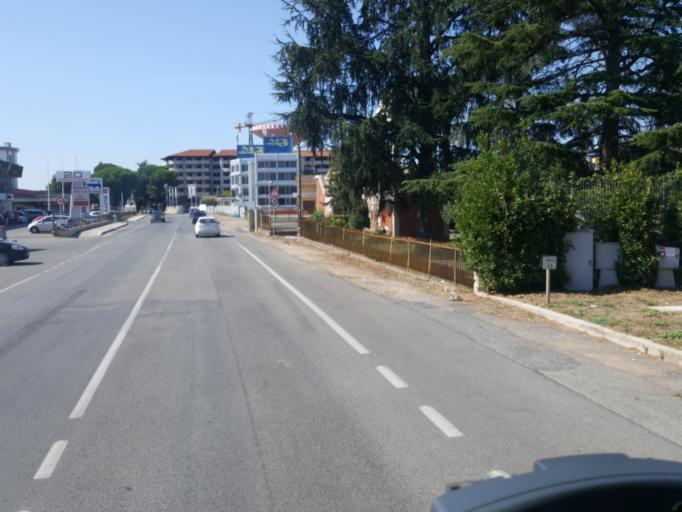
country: IT
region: Latium
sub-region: Citta metropolitana di Roma Capitale
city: Area Produttiva
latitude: 41.6875
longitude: 12.5138
